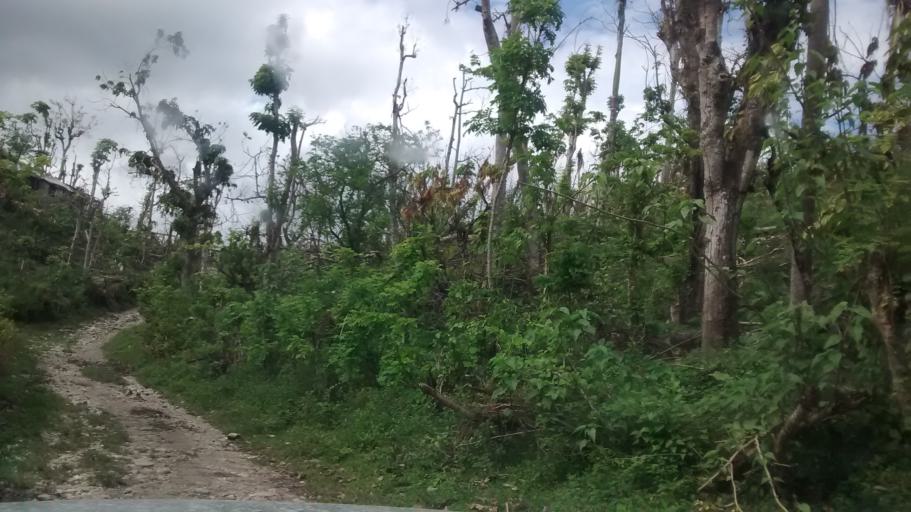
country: HT
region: Grandans
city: Moron
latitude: 18.5579
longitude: -74.2692
